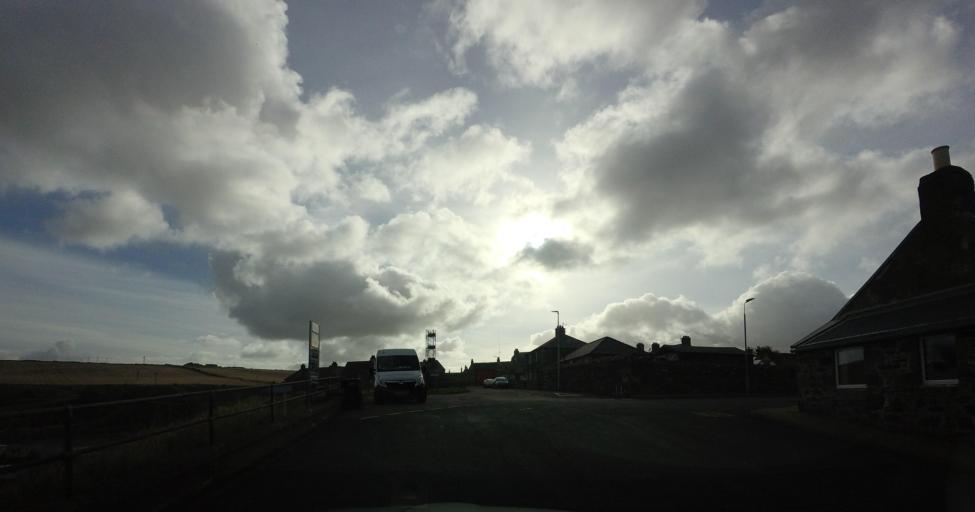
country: GB
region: Scotland
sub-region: Aberdeenshire
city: Portsoy
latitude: 57.6829
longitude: -2.6878
